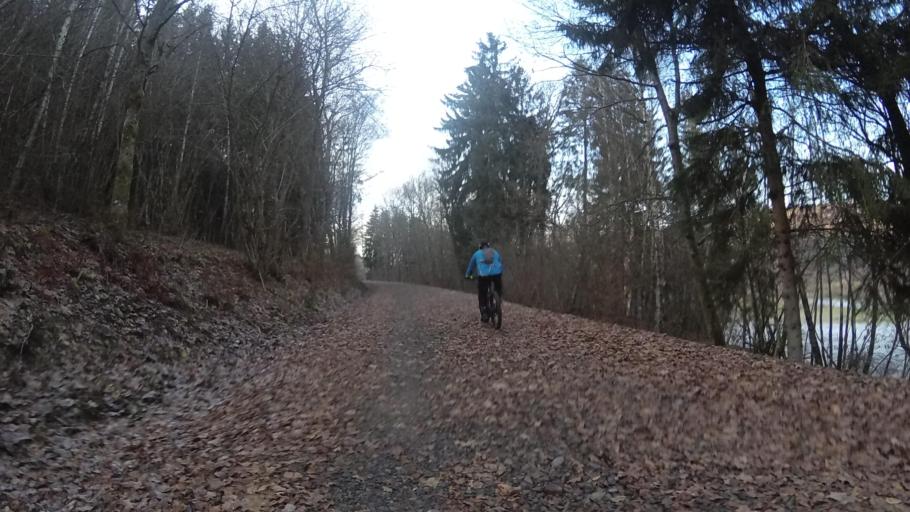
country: DE
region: Saarland
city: Nohfelden
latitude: 49.5748
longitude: 7.1592
